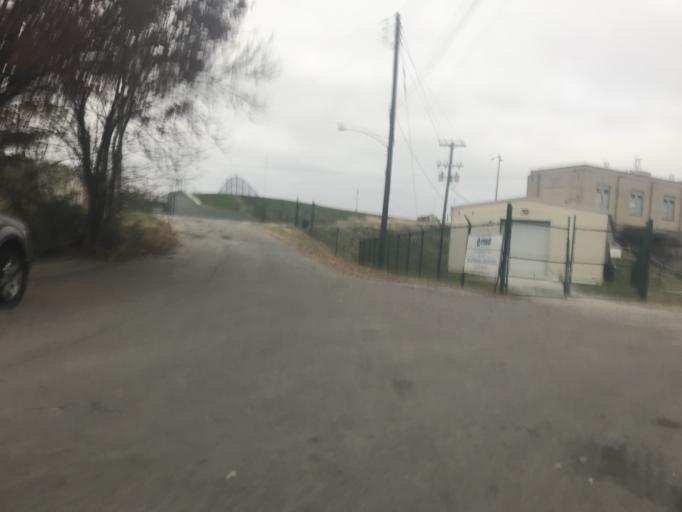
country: US
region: Indiana
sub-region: Clark County
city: Jeffersonville
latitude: 38.2608
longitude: -85.7191
